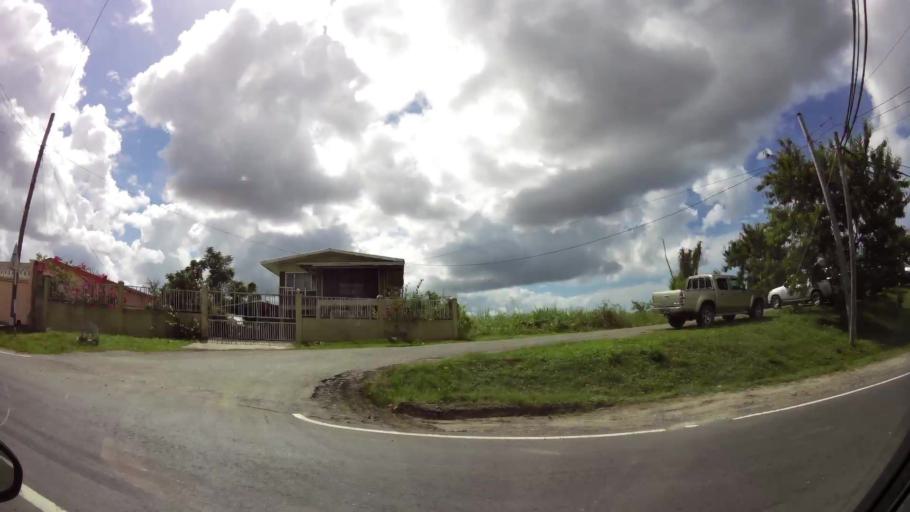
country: TT
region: City of San Fernando
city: San Fernando
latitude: 10.2448
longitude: -61.4975
